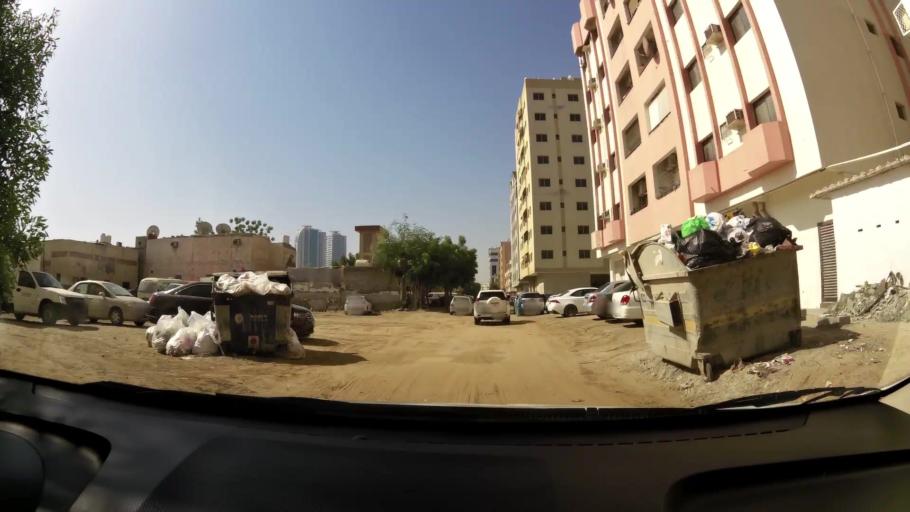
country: AE
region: Ajman
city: Ajman
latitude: 25.4097
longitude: 55.4472
